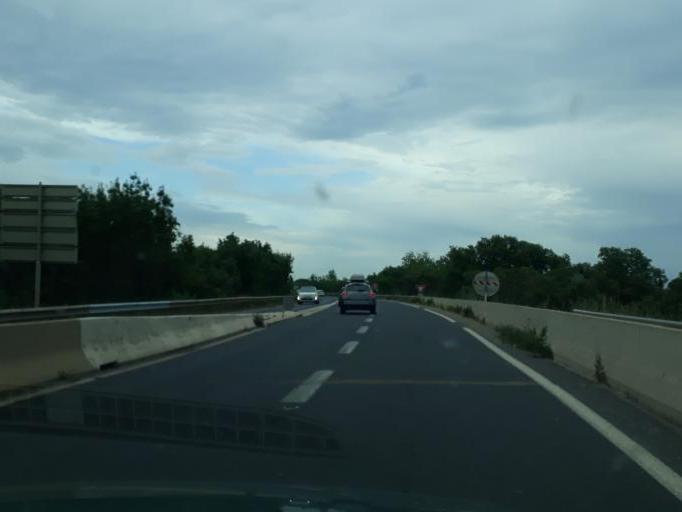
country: FR
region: Languedoc-Roussillon
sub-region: Departement de l'Herault
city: Vias
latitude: 43.3081
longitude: 3.4356
